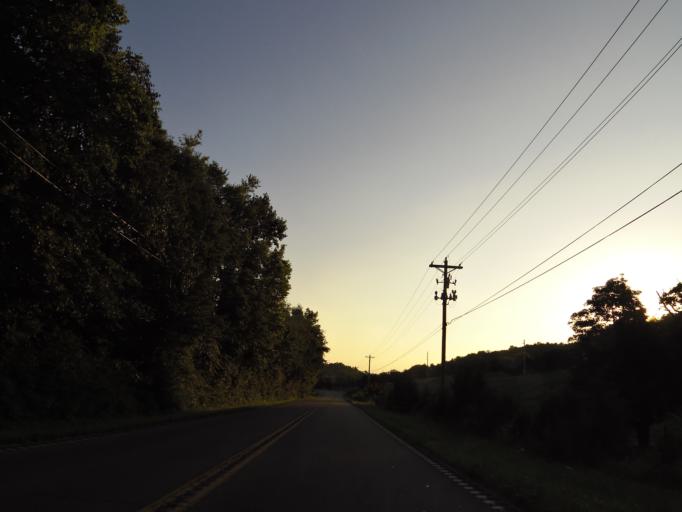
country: US
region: Tennessee
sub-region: Jefferson County
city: Dandridge
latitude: 36.0239
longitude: -83.4664
